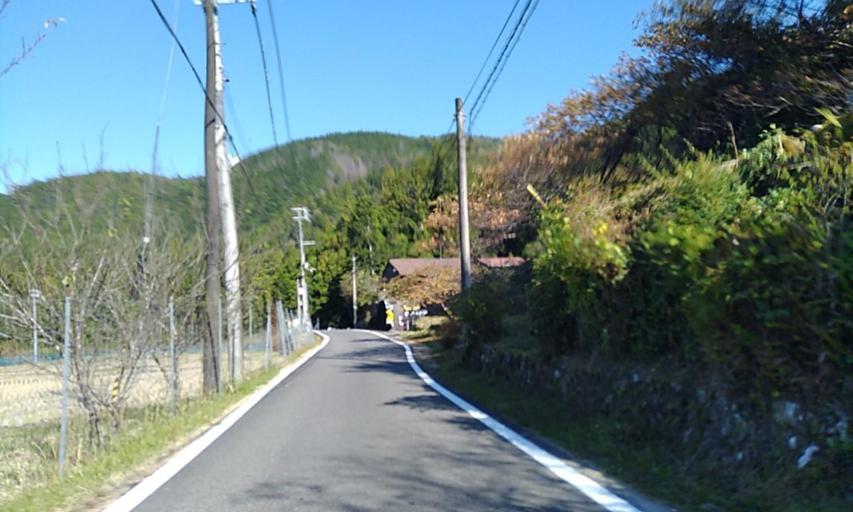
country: JP
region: Wakayama
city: Shingu
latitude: 33.9299
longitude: 135.9794
